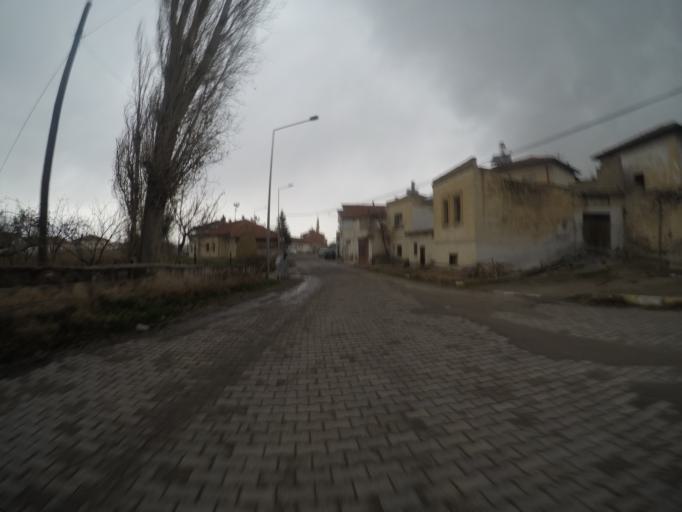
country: TR
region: Nevsehir
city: Goereme
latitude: 38.6685
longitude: 34.8419
